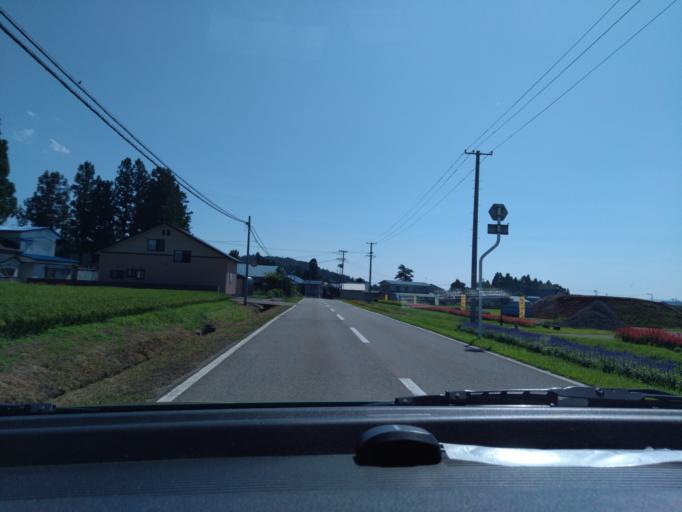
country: JP
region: Akita
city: Kakunodatemachi
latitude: 39.4770
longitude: 140.6113
